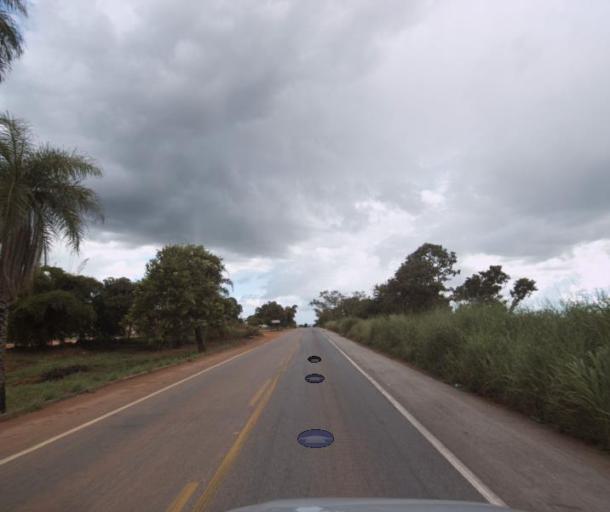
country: BR
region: Goias
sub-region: Porangatu
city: Porangatu
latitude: -13.3164
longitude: -49.1180
